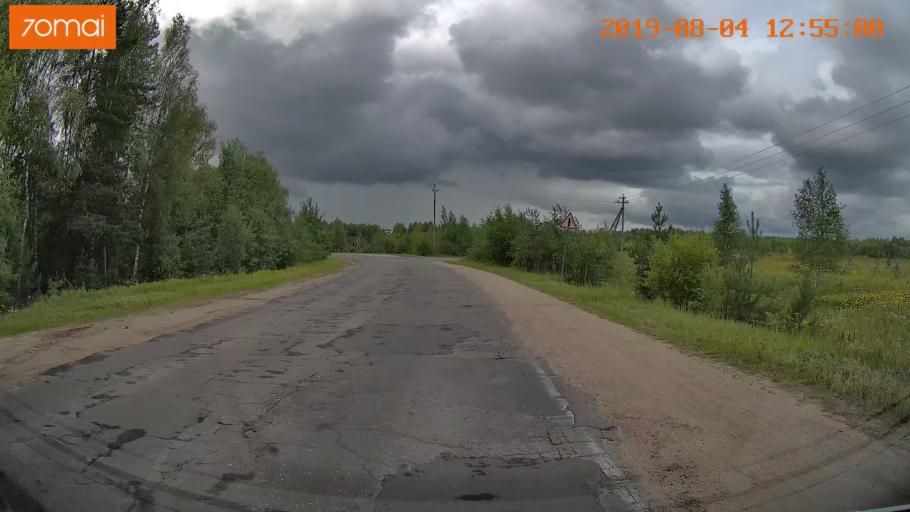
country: RU
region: Ivanovo
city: Novo-Talitsy
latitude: 57.0470
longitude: 40.8519
